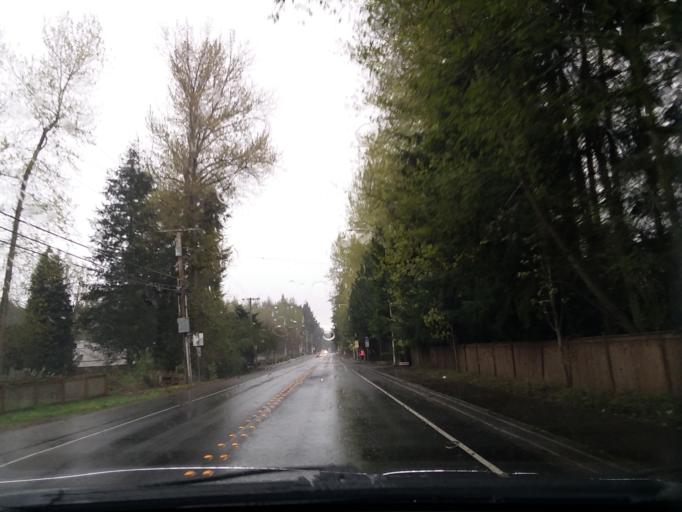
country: US
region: Washington
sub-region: King County
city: East Renton Highlands
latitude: 47.4838
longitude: -122.1484
